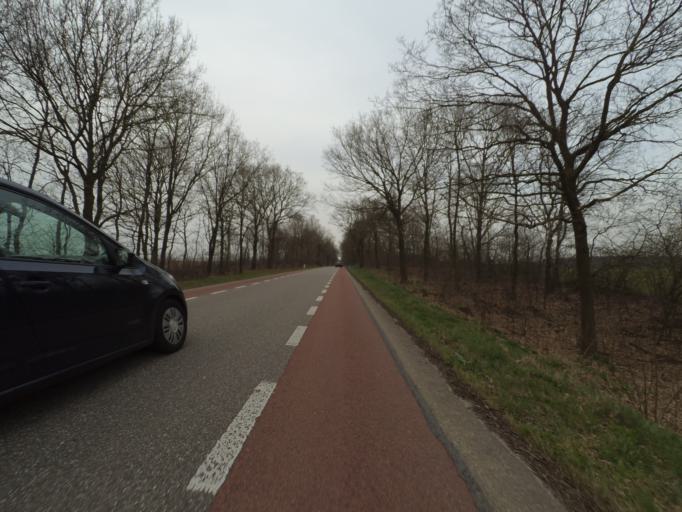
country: NL
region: Gelderland
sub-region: Gemeente Arnhem
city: Hoogkamp
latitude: 52.0898
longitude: 5.8792
